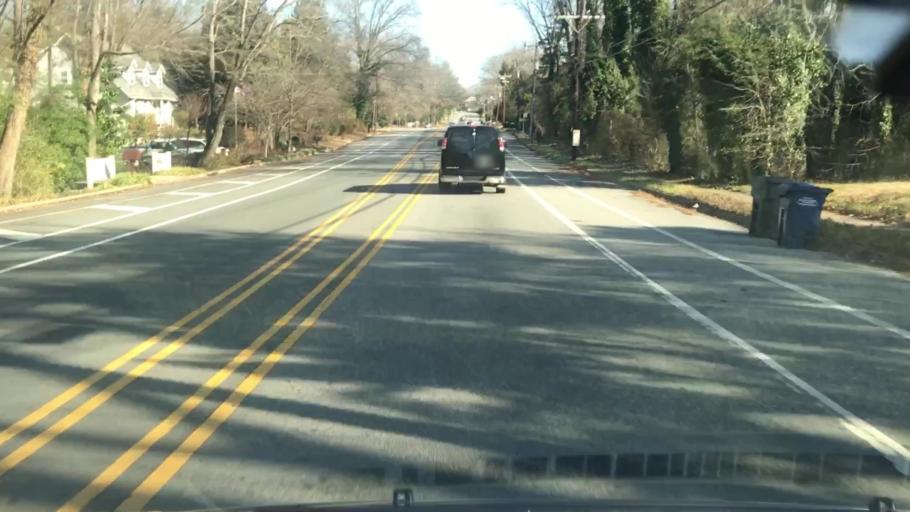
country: US
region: Virginia
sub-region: Fairfax County
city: Hybla Valley
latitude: 38.7452
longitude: -77.0713
